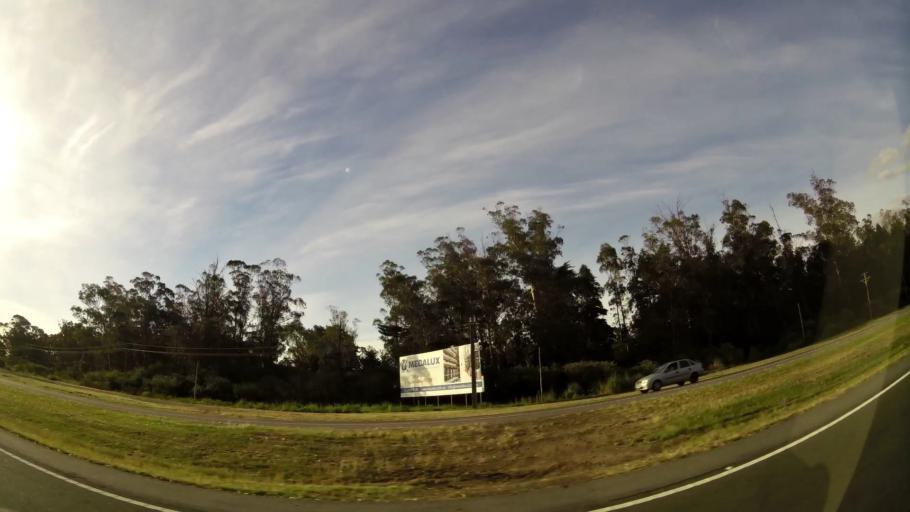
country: UY
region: Maldonado
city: Piriapolis
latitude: -34.7849
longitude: -55.3670
